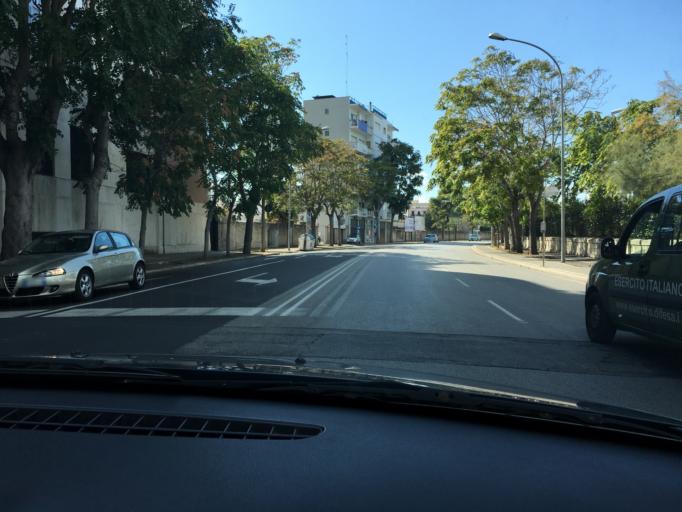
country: IT
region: Apulia
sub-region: Provincia di Bari
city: Bari
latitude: 41.1281
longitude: 16.8555
